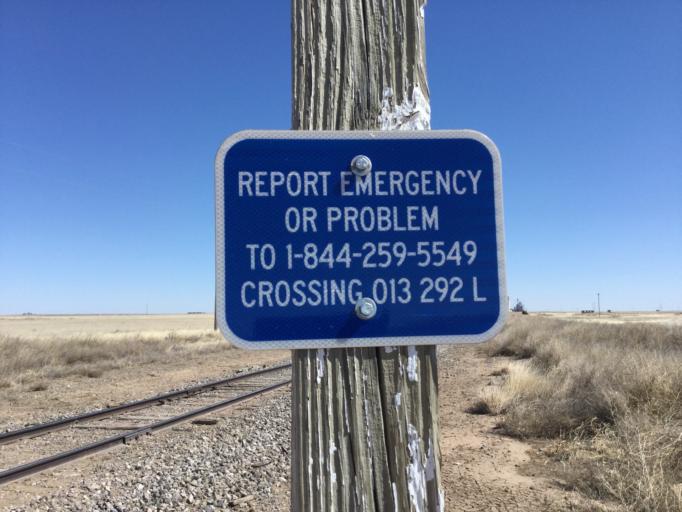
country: US
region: Kansas
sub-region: Grant County
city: Ulysses
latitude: 37.5722
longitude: -101.2538
